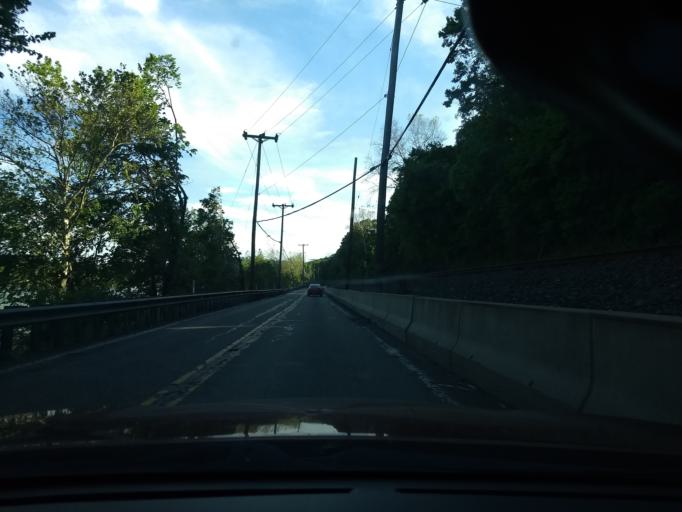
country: US
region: Pennsylvania
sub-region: Allegheny County
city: Glassport
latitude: 40.3310
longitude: -79.8977
